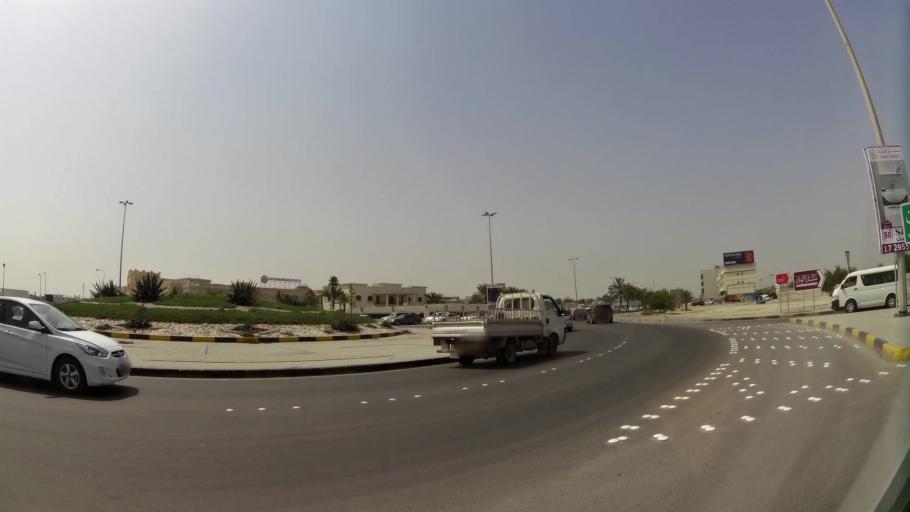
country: BH
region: Manama
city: Jidd Hafs
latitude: 26.2206
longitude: 50.4992
